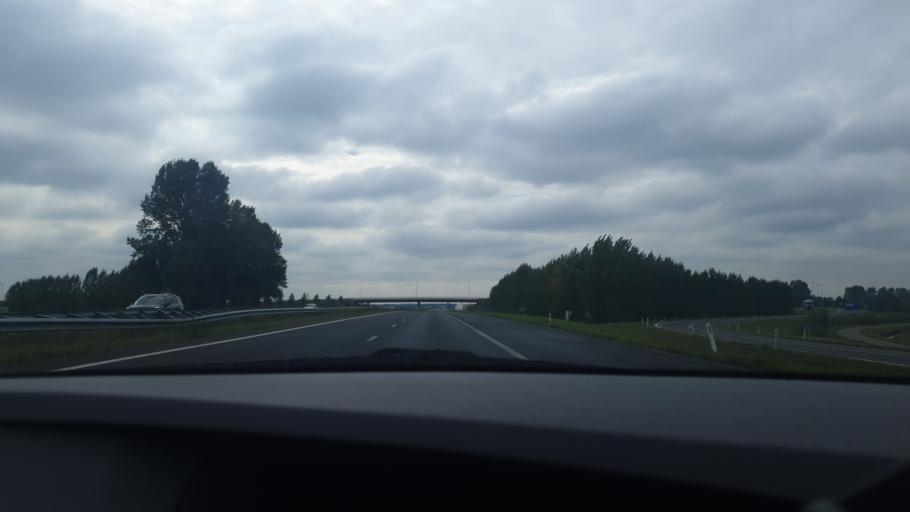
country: NL
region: North Brabant
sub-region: Gemeente Steenbergen
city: Dinteloord
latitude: 51.6275
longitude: 4.3836
